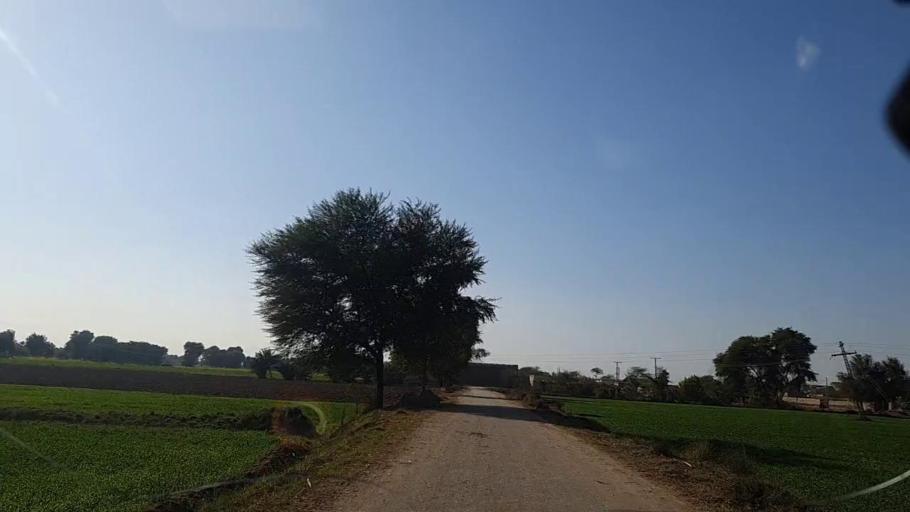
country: PK
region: Sindh
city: Khanpur
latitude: 27.7785
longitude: 69.3578
